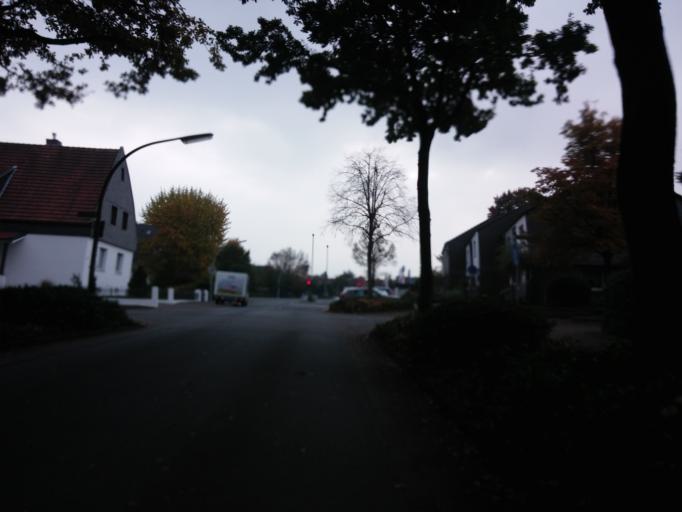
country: DE
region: North Rhine-Westphalia
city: Dorsten
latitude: 51.6579
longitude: 6.9513
